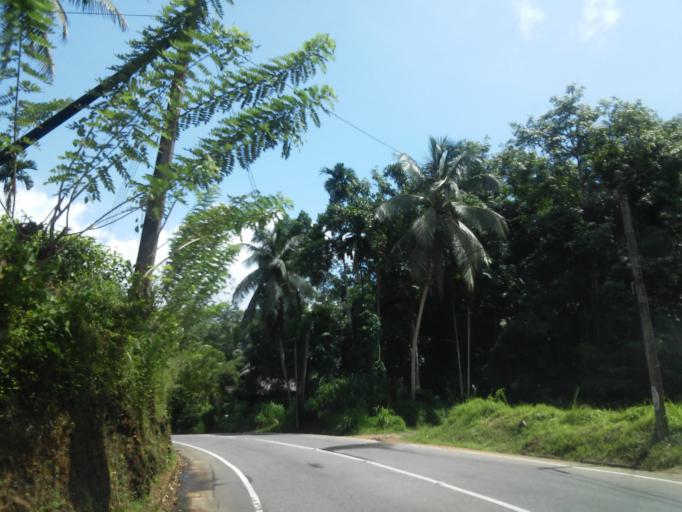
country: LK
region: Sabaragamuwa
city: Ratnapura
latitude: 6.7284
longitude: 80.3203
